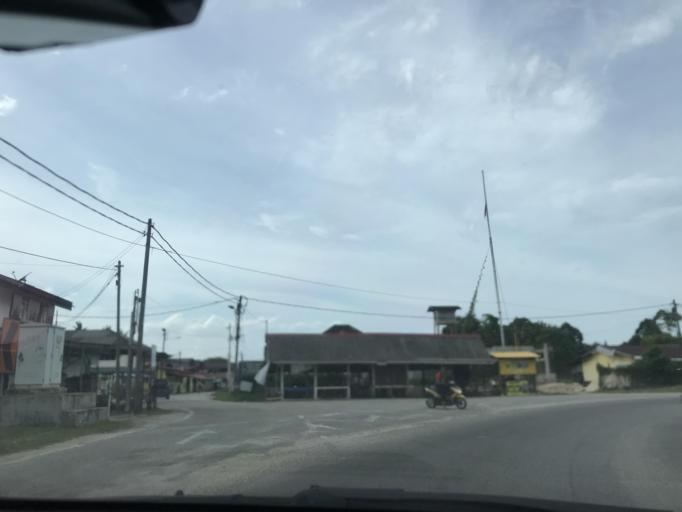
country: MY
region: Kelantan
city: Kota Bharu
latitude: 6.1024
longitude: 102.2309
